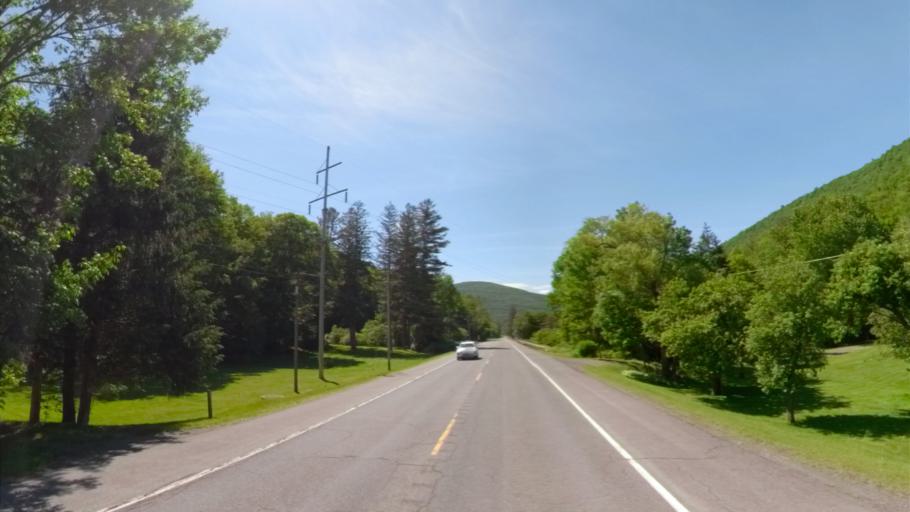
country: US
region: New York
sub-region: Ulster County
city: Shokan
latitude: 42.1154
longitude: -74.4557
